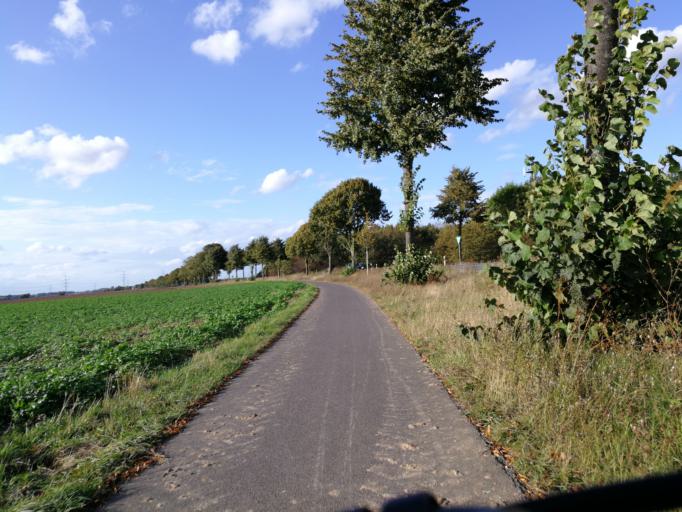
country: DE
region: North Rhine-Westphalia
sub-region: Regierungsbezirk Dusseldorf
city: Neubrueck
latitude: 51.1143
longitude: 6.7137
